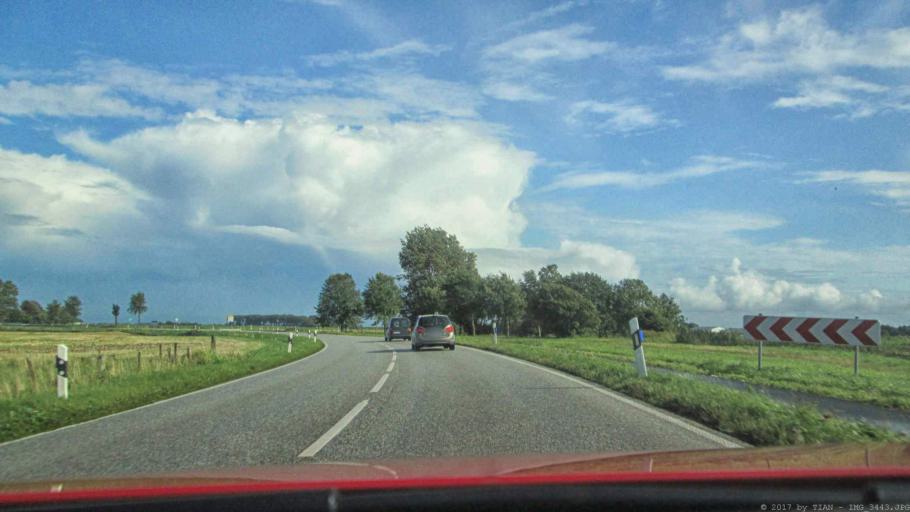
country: DE
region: Schleswig-Holstein
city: Wesselburener Deichhausen
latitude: 54.1522
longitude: 8.9152
